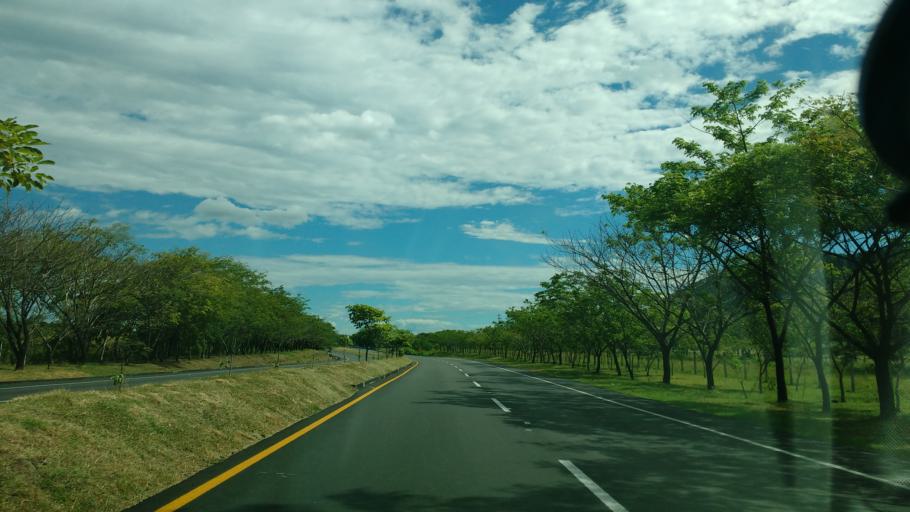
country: CO
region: Tolima
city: Espinal
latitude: 4.2247
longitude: -74.9376
